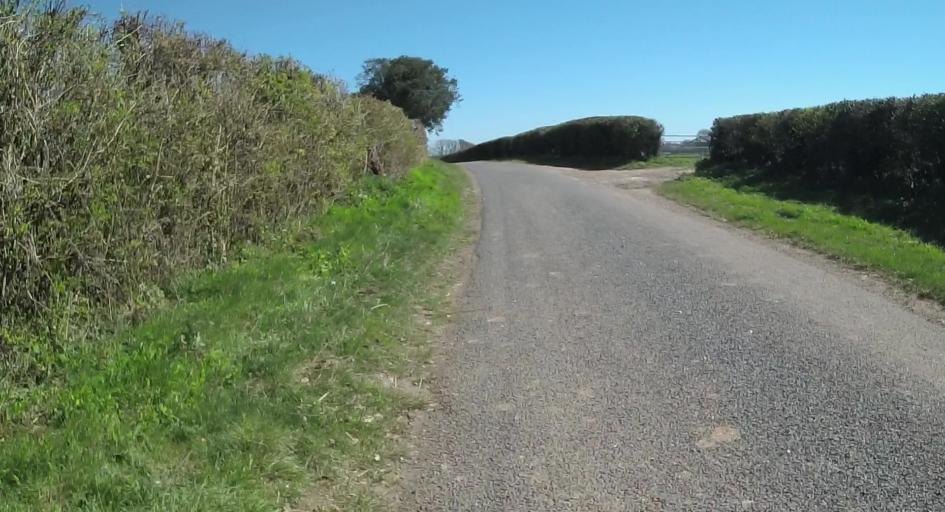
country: GB
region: England
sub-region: Hampshire
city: Old Basing
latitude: 51.2463
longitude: -1.0362
